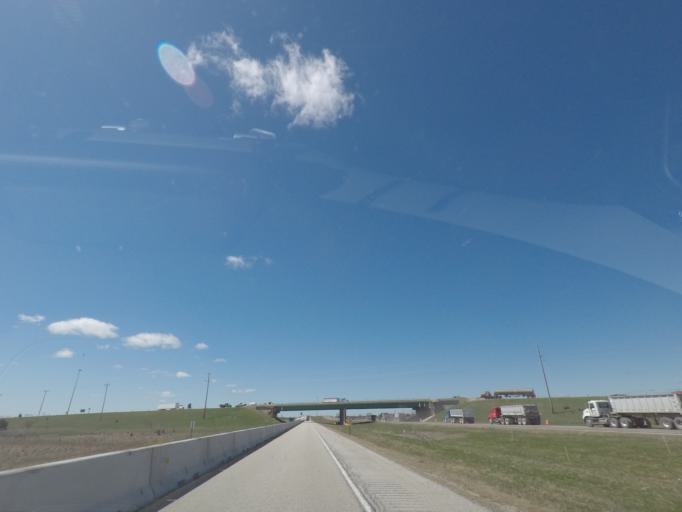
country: US
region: Illinois
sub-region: Livingston County
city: Pontiac
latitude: 40.9190
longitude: -88.6414
